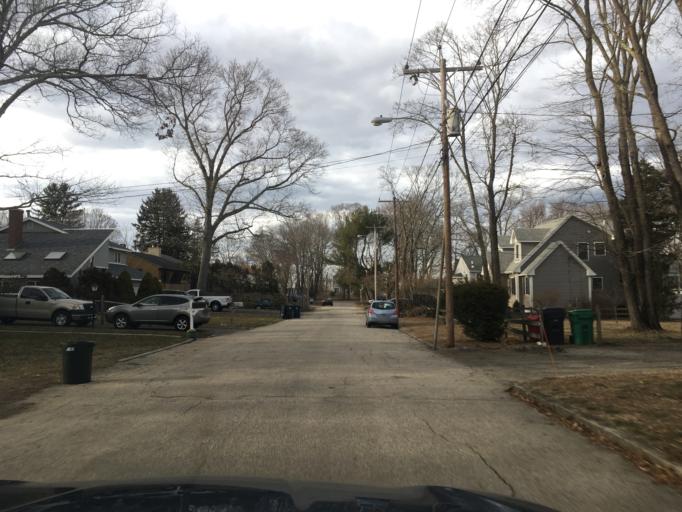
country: US
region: Rhode Island
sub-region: Kent County
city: Warwick
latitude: 41.6633
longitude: -71.4191
